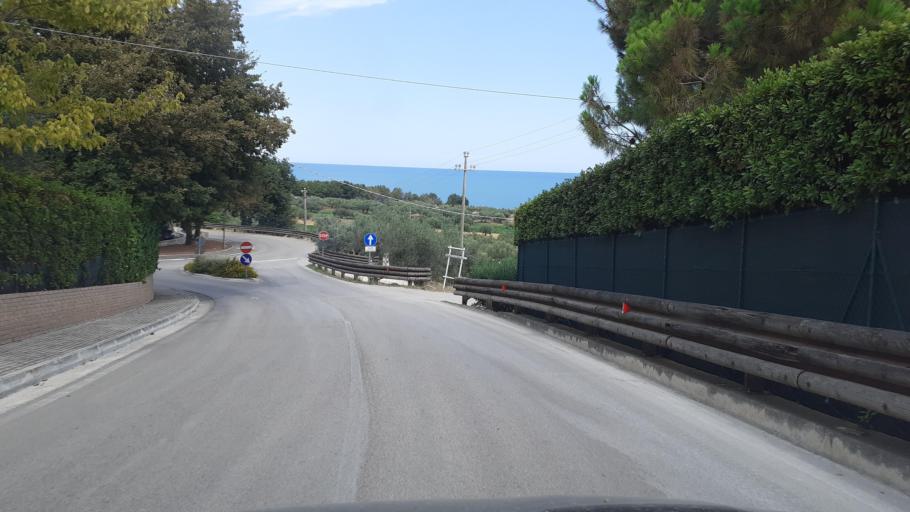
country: IT
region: Abruzzo
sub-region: Provincia di Chieti
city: Fossacesia
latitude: 42.2526
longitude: 14.4979
